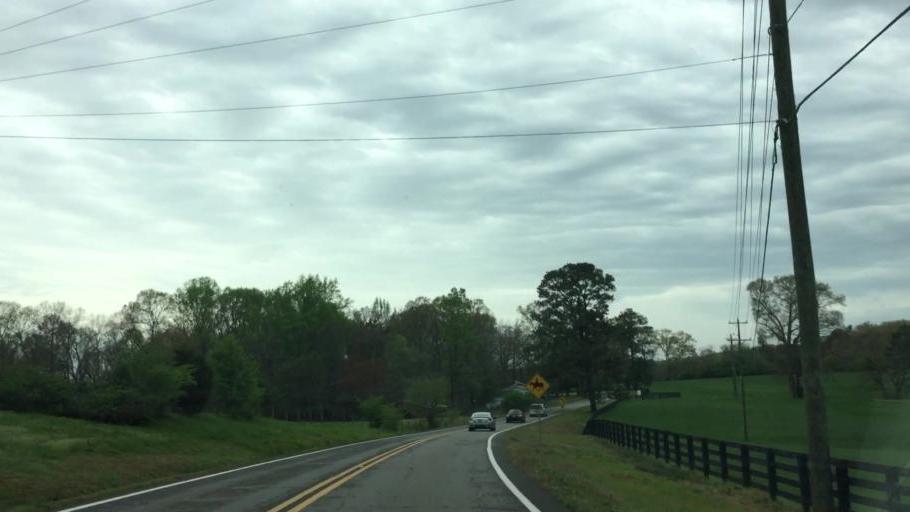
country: US
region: Georgia
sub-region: Fulton County
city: Milton
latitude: 34.1845
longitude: -84.3407
